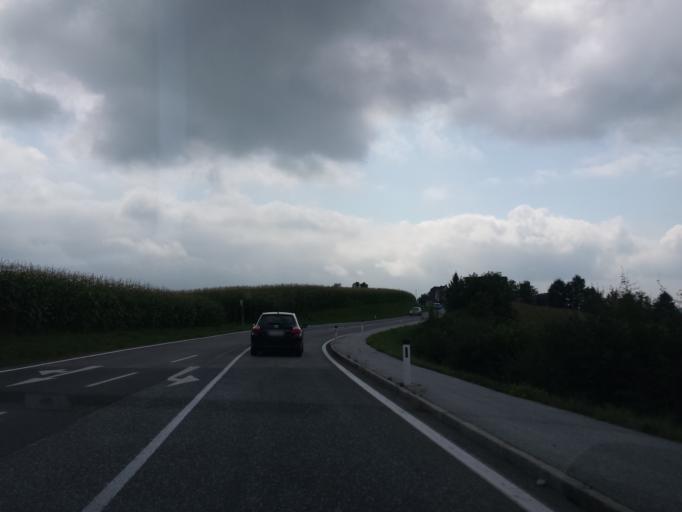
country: AT
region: Styria
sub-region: Politischer Bezirk Deutschlandsberg
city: Rassach
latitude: 46.8630
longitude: 15.2656
